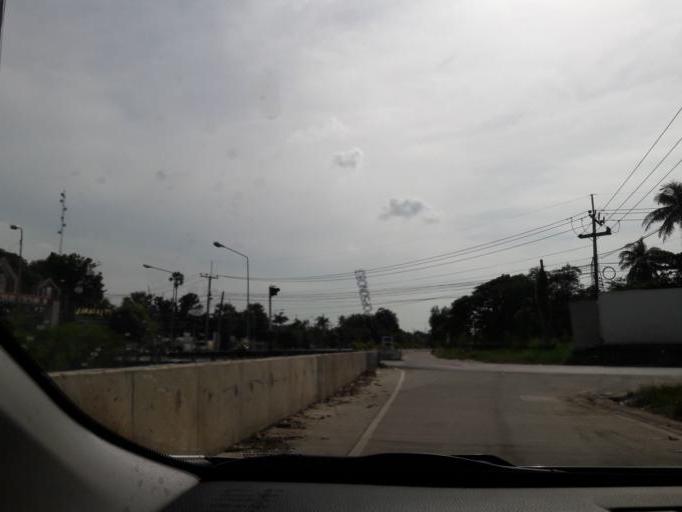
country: TH
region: Ang Thong
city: Ang Thong
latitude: 14.5909
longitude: 100.4460
